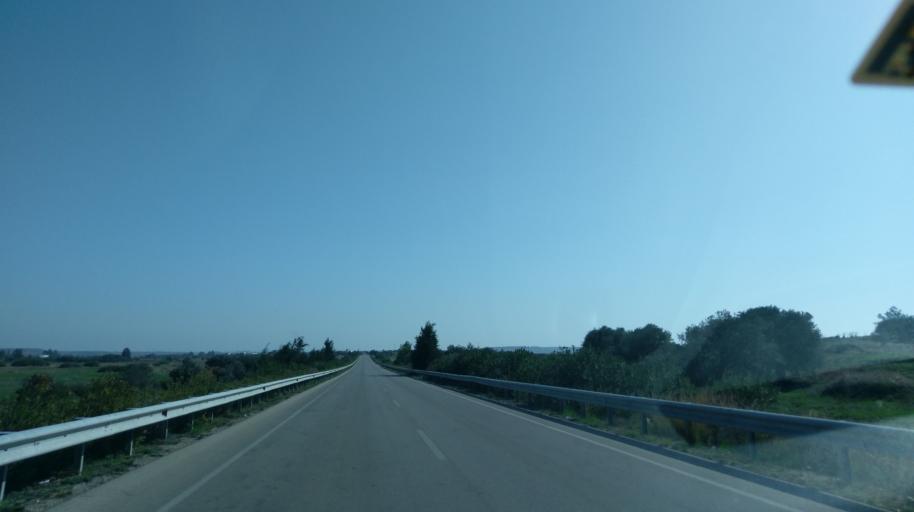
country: CY
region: Ammochostos
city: Leonarisso
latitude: 35.3973
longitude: 34.0014
